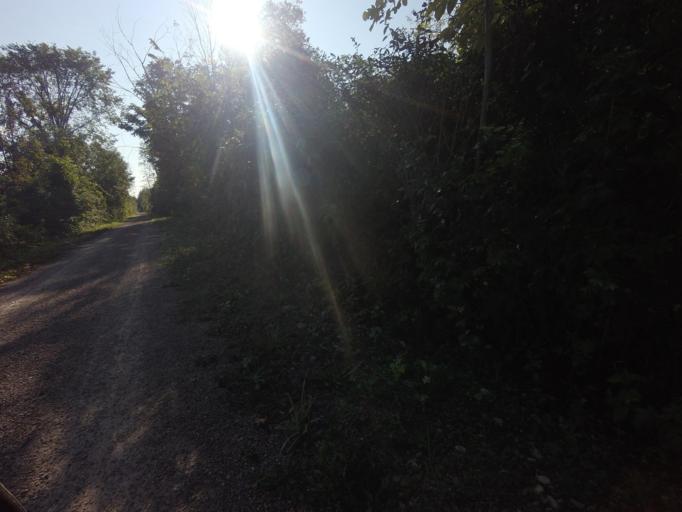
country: CA
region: Ontario
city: Huron East
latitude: 43.7376
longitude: -81.4570
